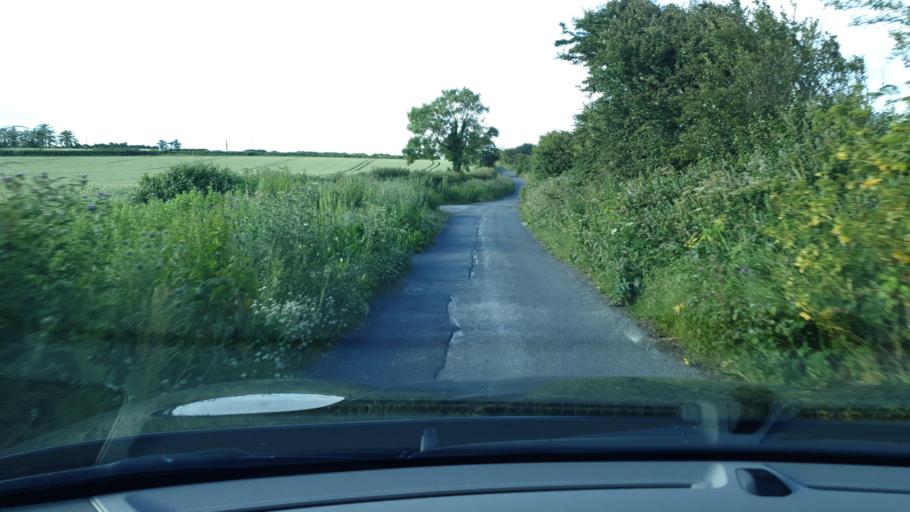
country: IE
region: Leinster
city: An Ros
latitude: 53.5487
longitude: -6.0857
